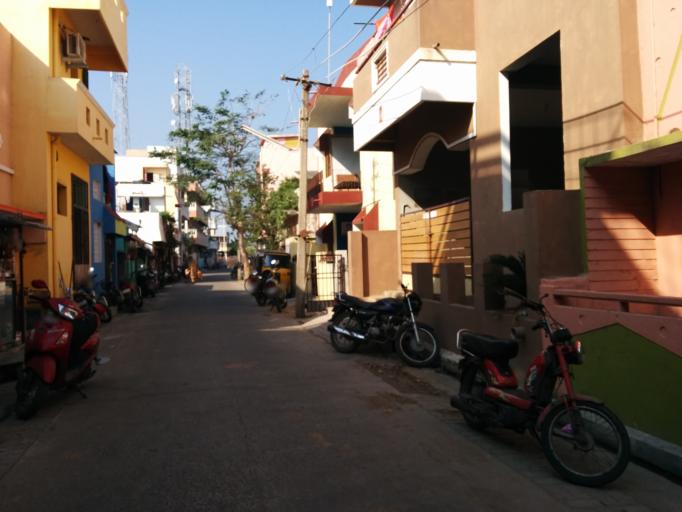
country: IN
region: Pondicherry
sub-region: Puducherry
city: Puducherry
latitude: 11.9489
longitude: 79.8350
